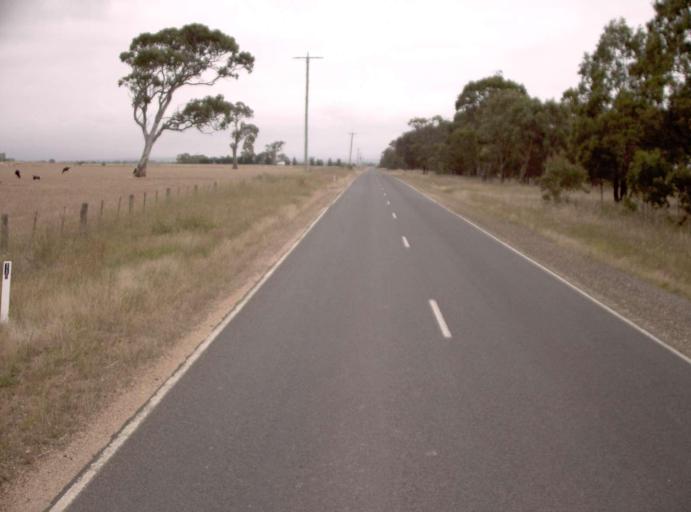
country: AU
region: Victoria
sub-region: Wellington
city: Heyfield
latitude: -38.0458
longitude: 146.7676
